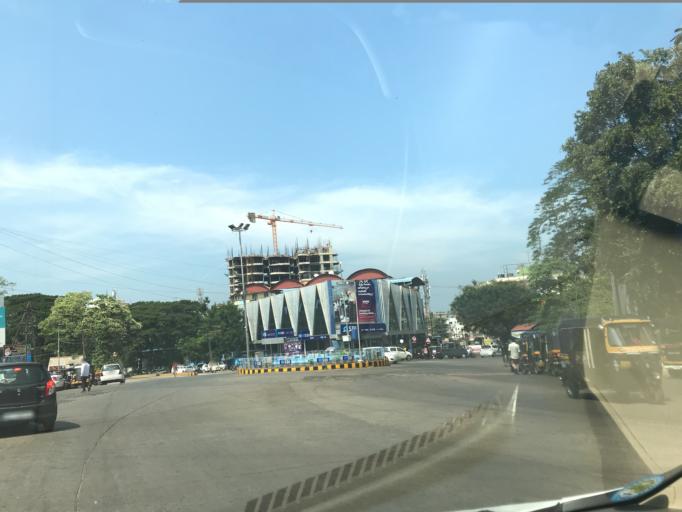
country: IN
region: Karnataka
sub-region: Dakshina Kannada
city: Ullal
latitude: 12.8614
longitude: 74.8376
